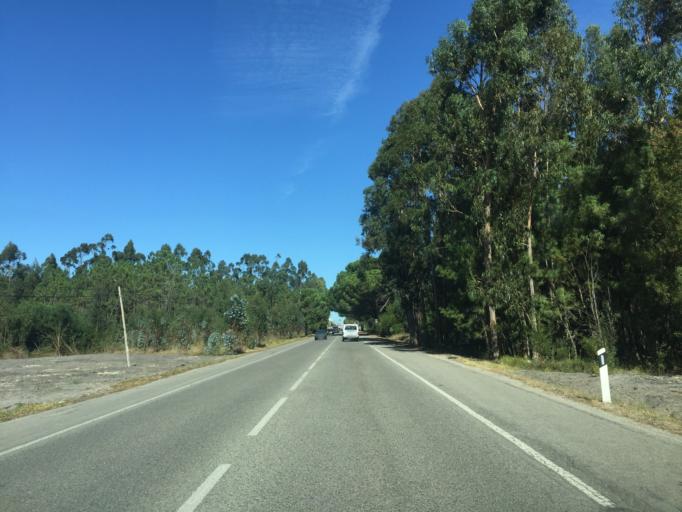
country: PT
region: Coimbra
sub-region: Figueira da Foz
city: Alhadas
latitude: 40.2946
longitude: -8.7637
